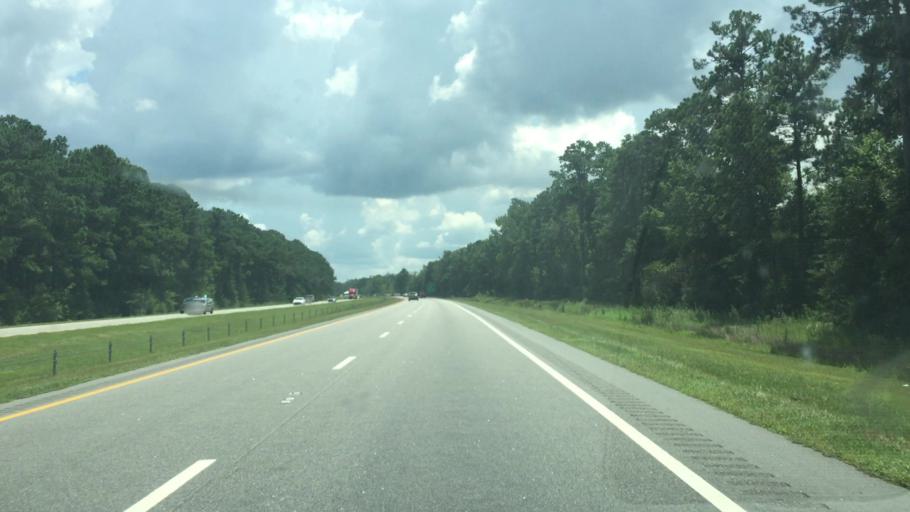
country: US
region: North Carolina
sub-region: Columbus County
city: Chadbourn
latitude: 34.4059
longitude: -78.9235
